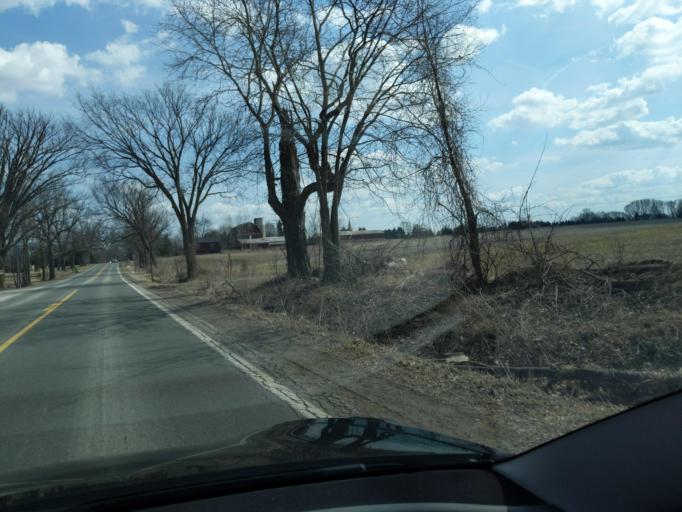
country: US
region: Michigan
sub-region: Washtenaw County
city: Dexter
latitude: 42.3842
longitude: -83.8840
